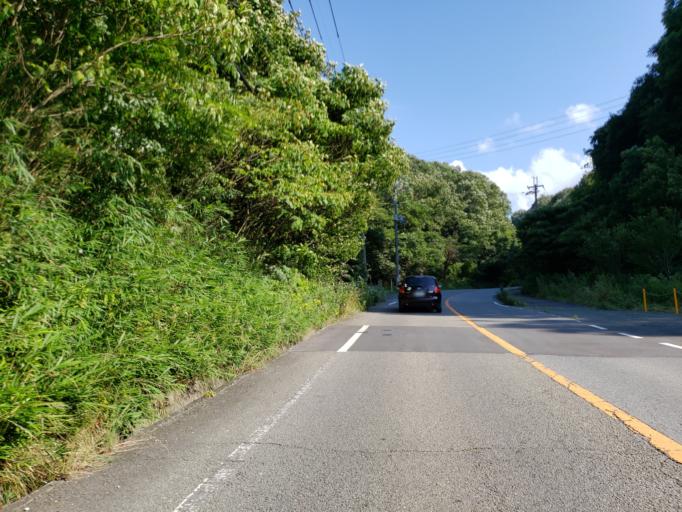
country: JP
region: Hyogo
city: Kakogawacho-honmachi
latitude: 34.8925
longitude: 134.8068
